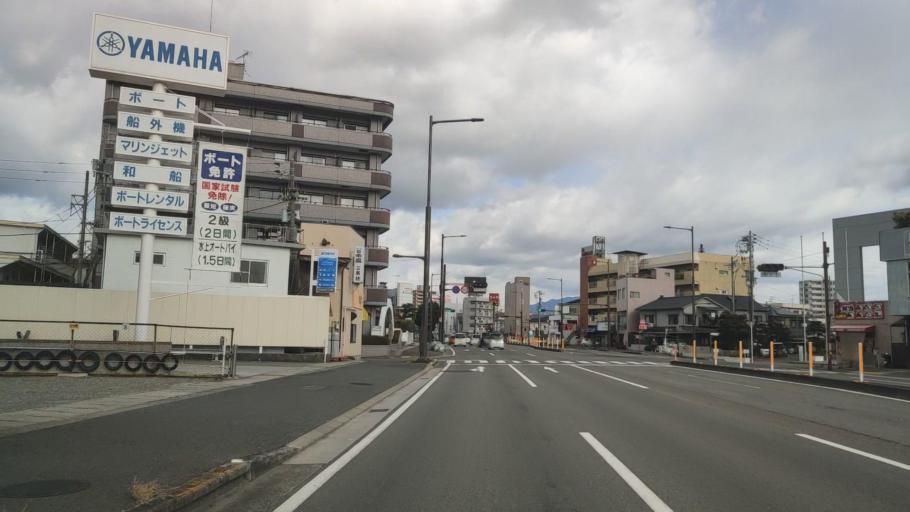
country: JP
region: Ehime
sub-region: Shikoku-chuo Shi
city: Matsuyama
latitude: 33.8241
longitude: 132.7577
